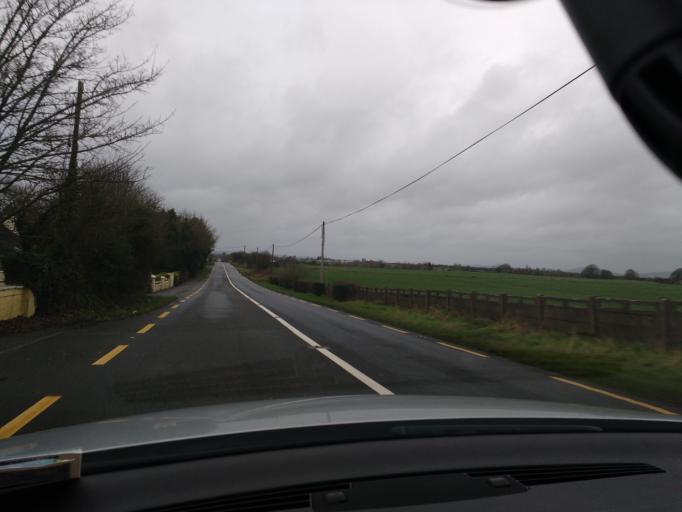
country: IE
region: Munster
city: Thurles
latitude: 52.6745
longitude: -7.7663
